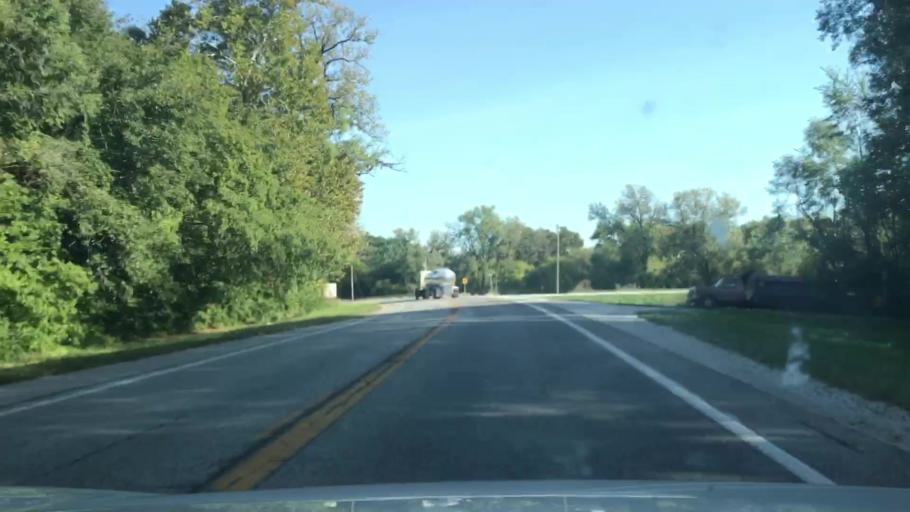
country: US
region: Illinois
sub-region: Adams County
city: Quincy
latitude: 39.8426
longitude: -91.3720
